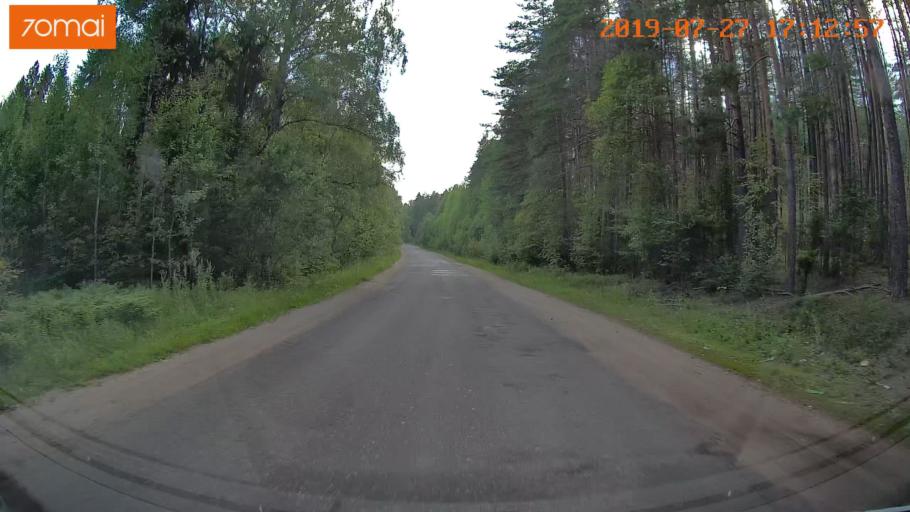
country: RU
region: Ivanovo
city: Novo-Talitsy
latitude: 57.0547
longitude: 40.8573
